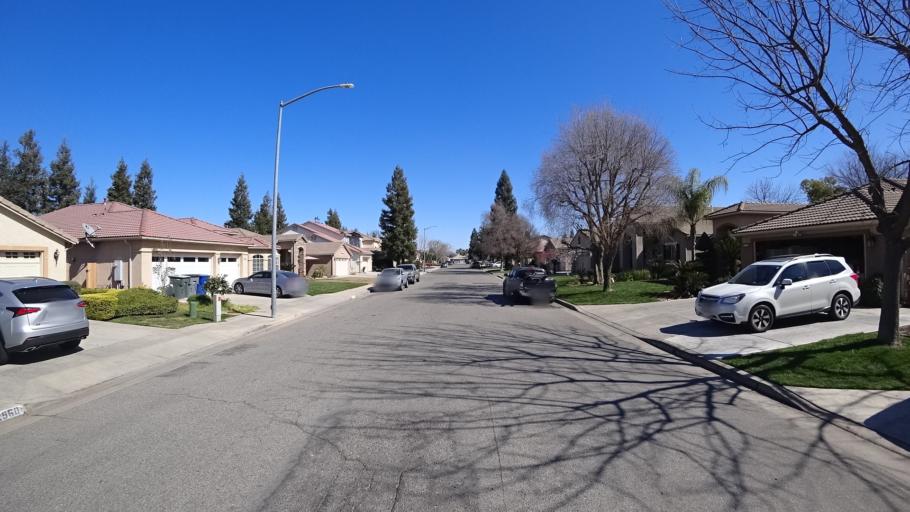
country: US
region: California
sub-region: Fresno County
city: Clovis
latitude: 36.8562
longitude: -119.7375
